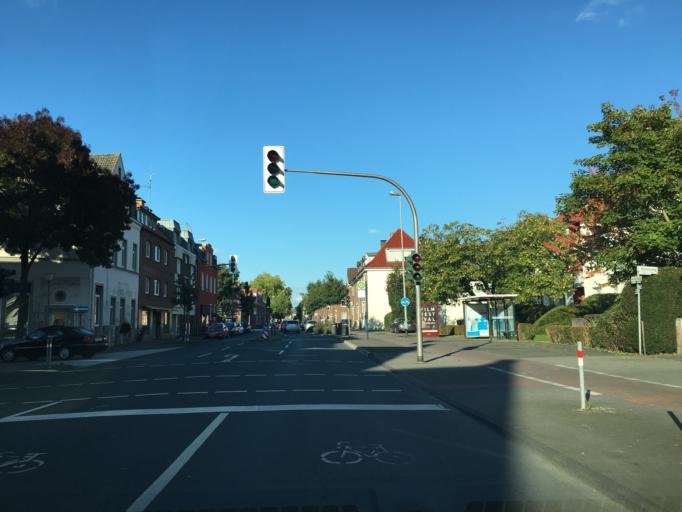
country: DE
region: North Rhine-Westphalia
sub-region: Regierungsbezirk Munster
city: Muenster
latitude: 51.9696
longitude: 7.6339
